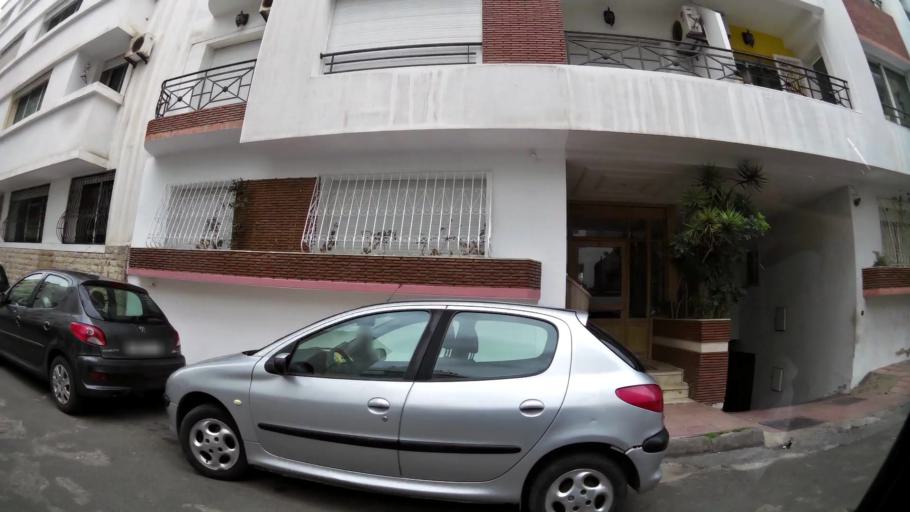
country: MA
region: Grand Casablanca
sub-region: Casablanca
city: Casablanca
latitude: 33.5916
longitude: -7.6444
